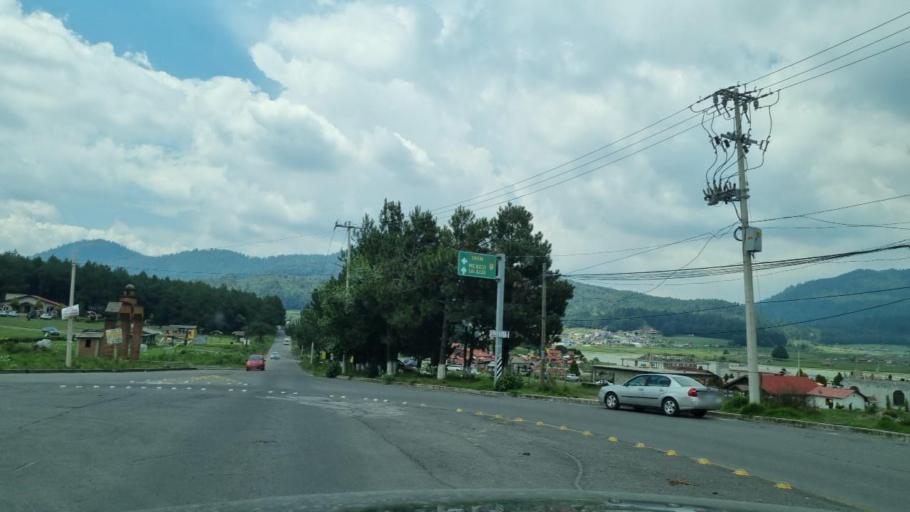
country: MX
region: Morelos
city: San Jeronimo Acazulco
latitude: 19.3005
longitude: -99.3914
